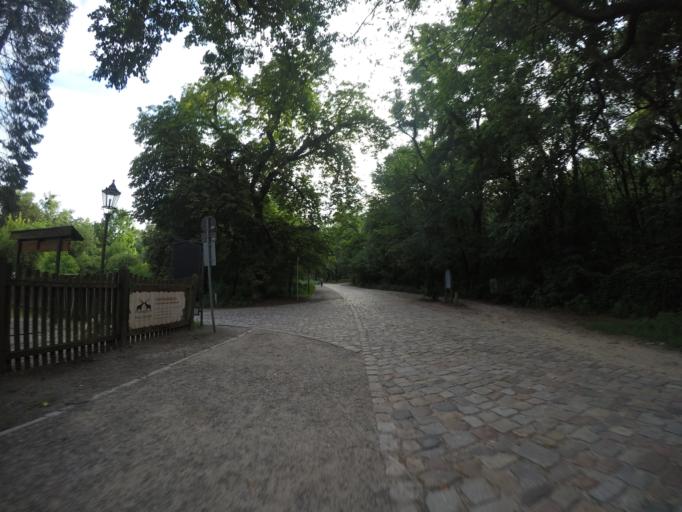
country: DE
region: Berlin
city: Grunewald
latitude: 52.4667
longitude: 13.2557
